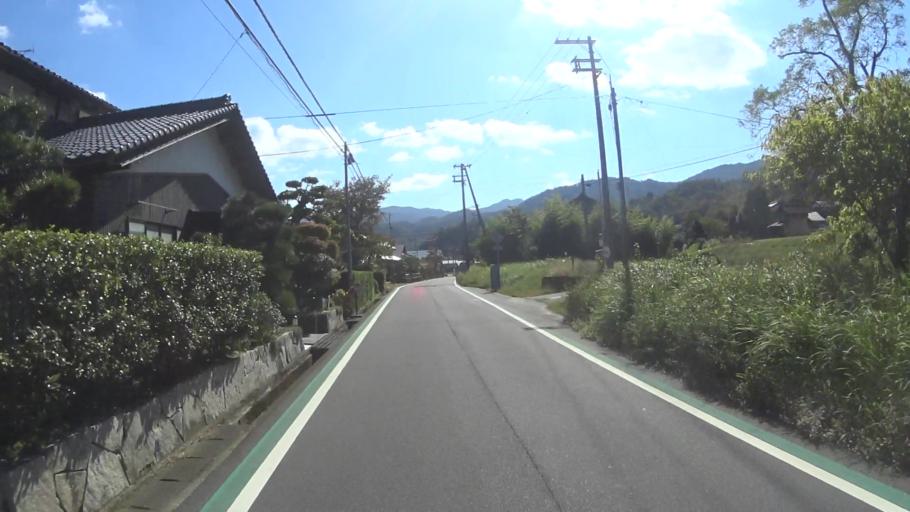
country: JP
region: Hyogo
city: Toyooka
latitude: 35.5596
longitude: 134.9312
